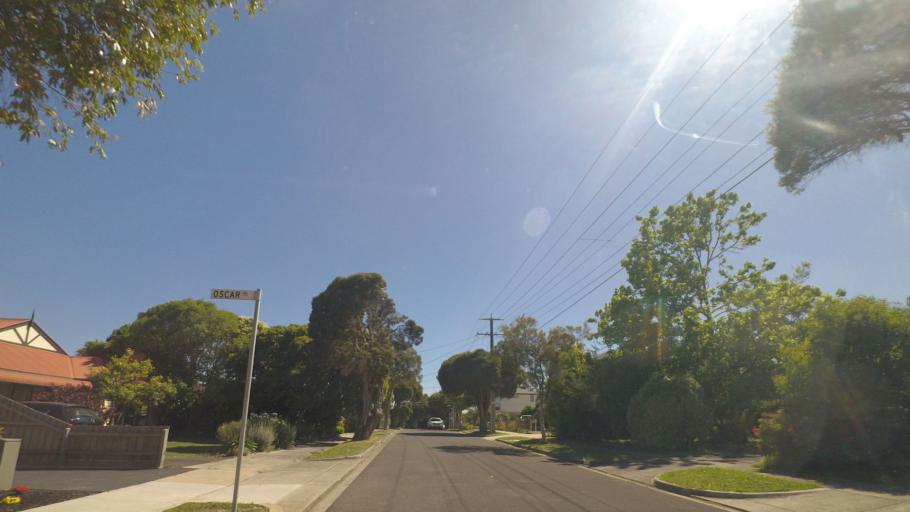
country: AU
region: Victoria
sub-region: Yarra Ranges
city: Kilsyth
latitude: -37.7999
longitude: 145.3102
